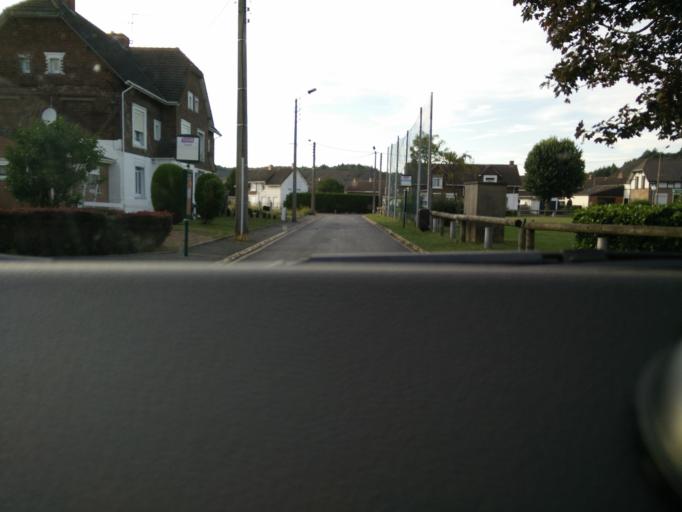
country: FR
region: Nord-Pas-de-Calais
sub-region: Departement du Pas-de-Calais
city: Grenay
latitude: 50.4529
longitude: 2.7462
